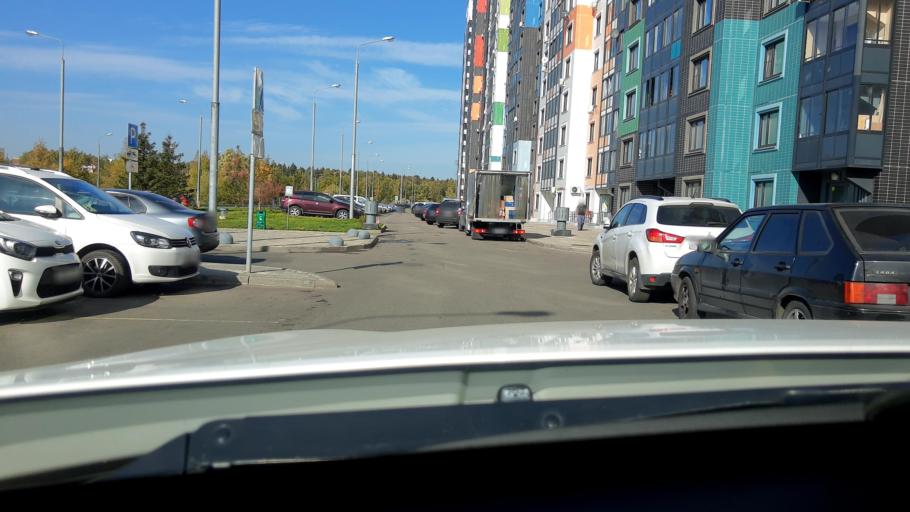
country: RU
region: Moscow
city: Severnyy
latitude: 55.9292
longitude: 37.5401
